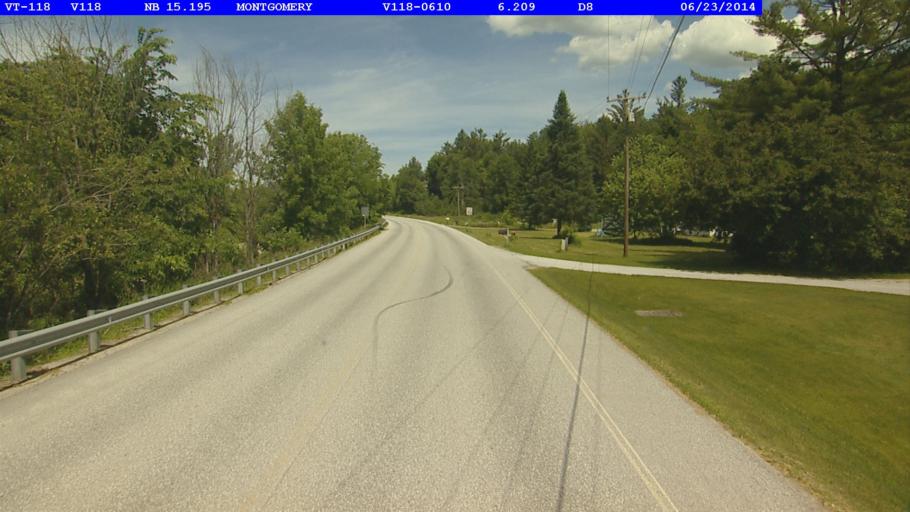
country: US
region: Vermont
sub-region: Franklin County
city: Richford
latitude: 44.8835
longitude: -72.6167
